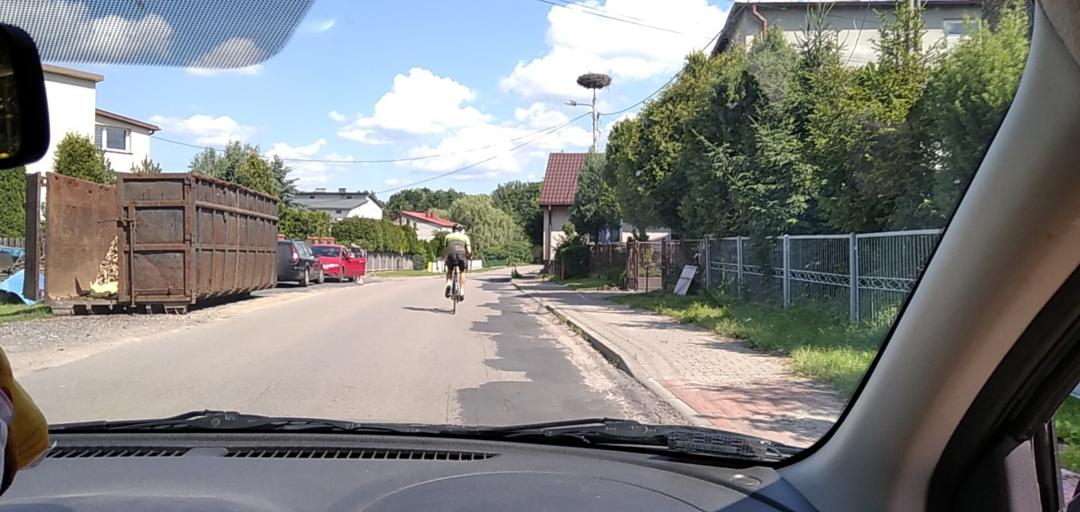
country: PL
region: Silesian Voivodeship
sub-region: Powiat bedzinski
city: Sarnow
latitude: 50.3864
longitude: 19.1374
